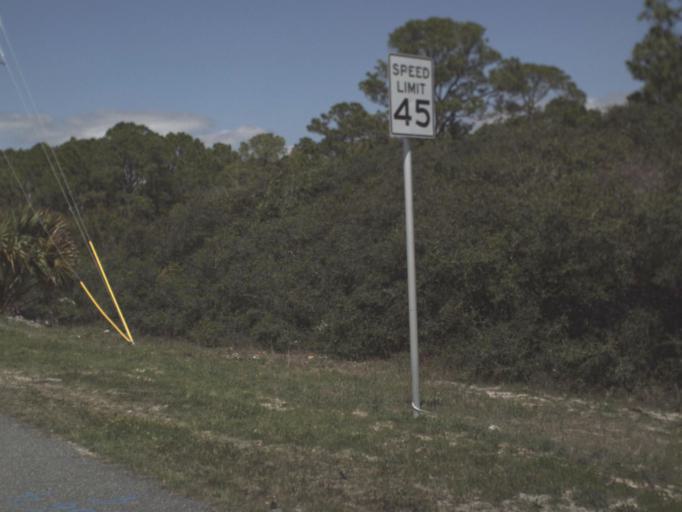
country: US
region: Florida
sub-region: Bay County
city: Mexico Beach
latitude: 29.8917
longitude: -85.3577
